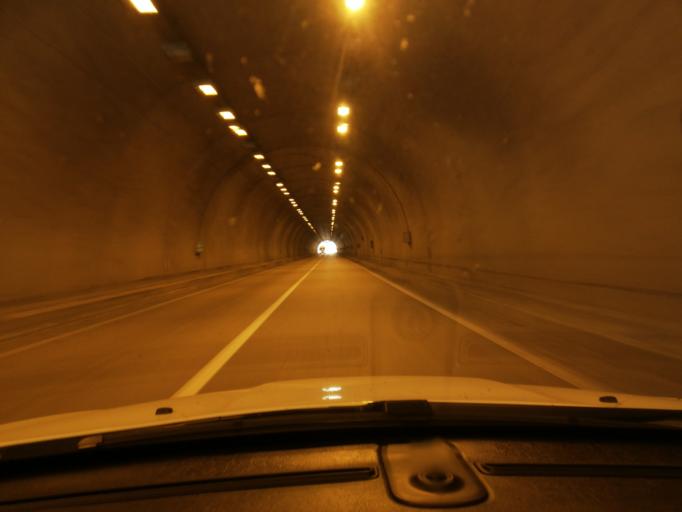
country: TR
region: Karabuk
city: Yenice
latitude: 41.2032
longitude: 32.4084
